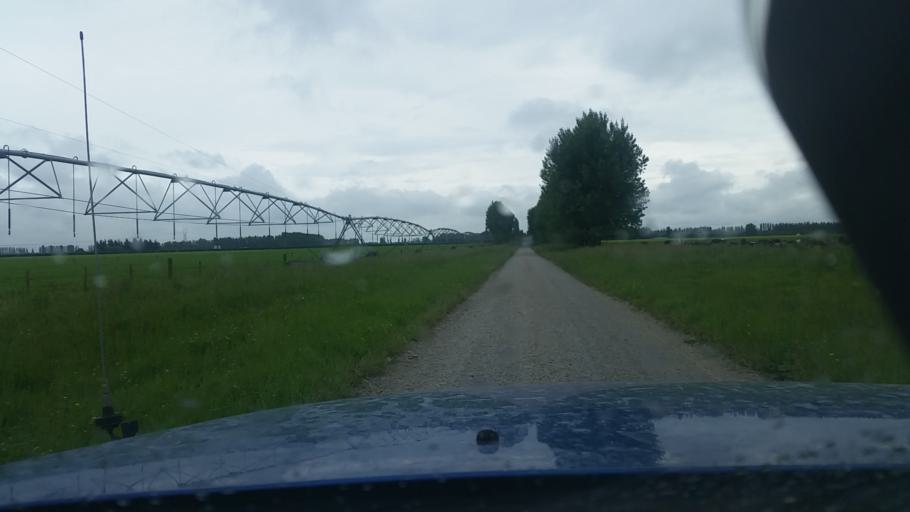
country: NZ
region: Canterbury
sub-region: Ashburton District
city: Ashburton
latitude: -43.8172
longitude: 171.6617
